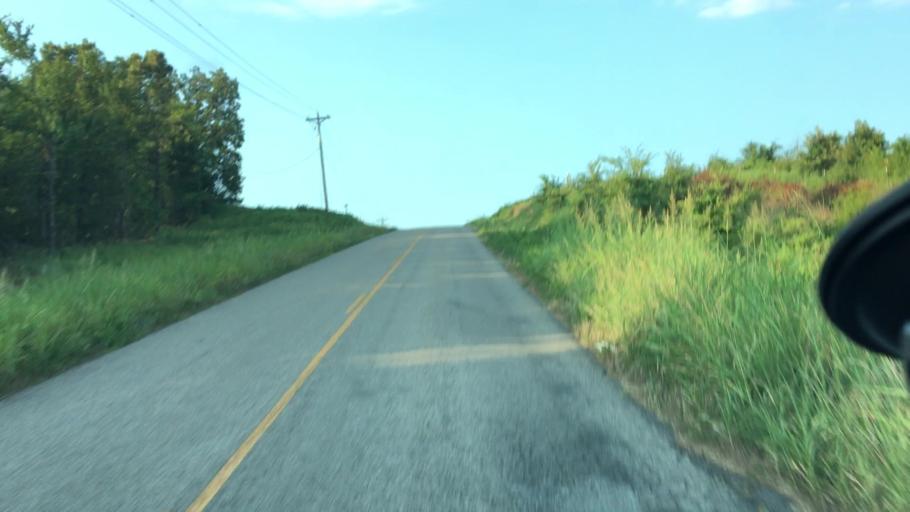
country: US
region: Arkansas
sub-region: Johnson County
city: Coal Hill
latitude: 35.3584
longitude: -93.6131
